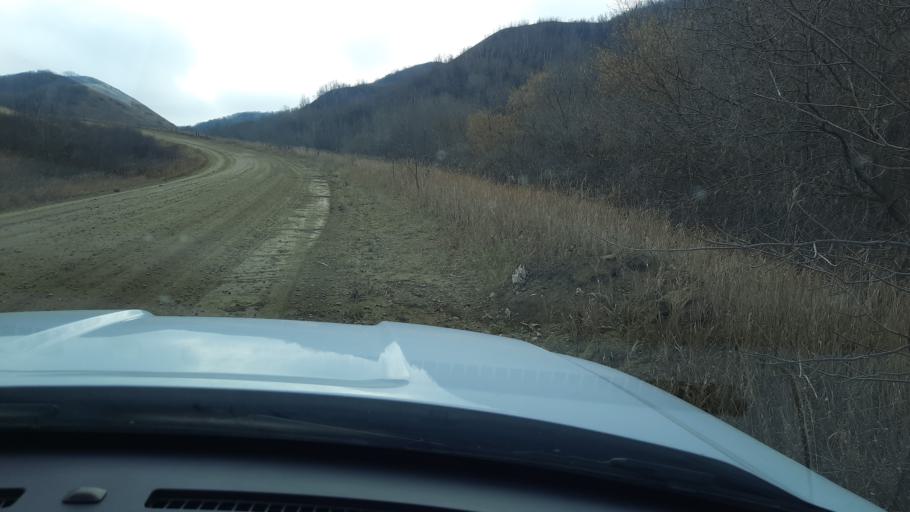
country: CA
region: Saskatchewan
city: White City
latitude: 50.7737
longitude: -104.1343
